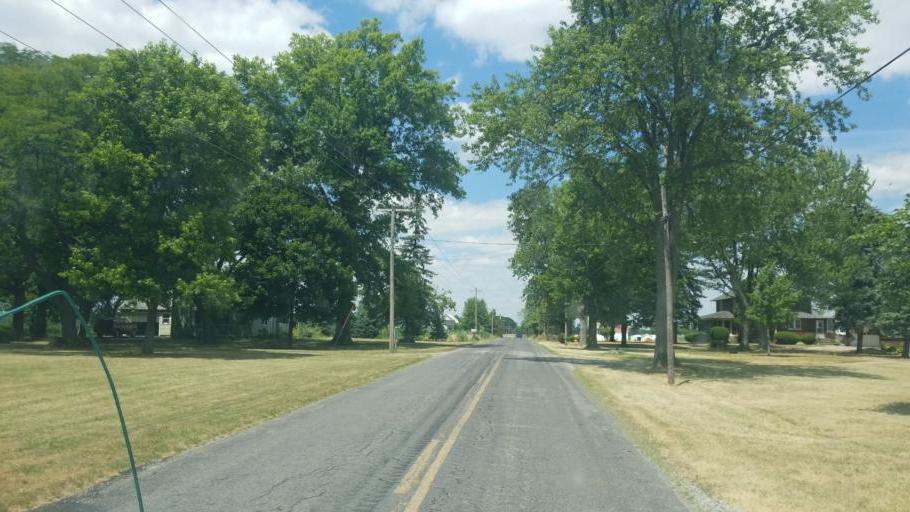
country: US
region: Ohio
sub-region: Williams County
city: Edgerton
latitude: 41.4355
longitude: -84.7102
